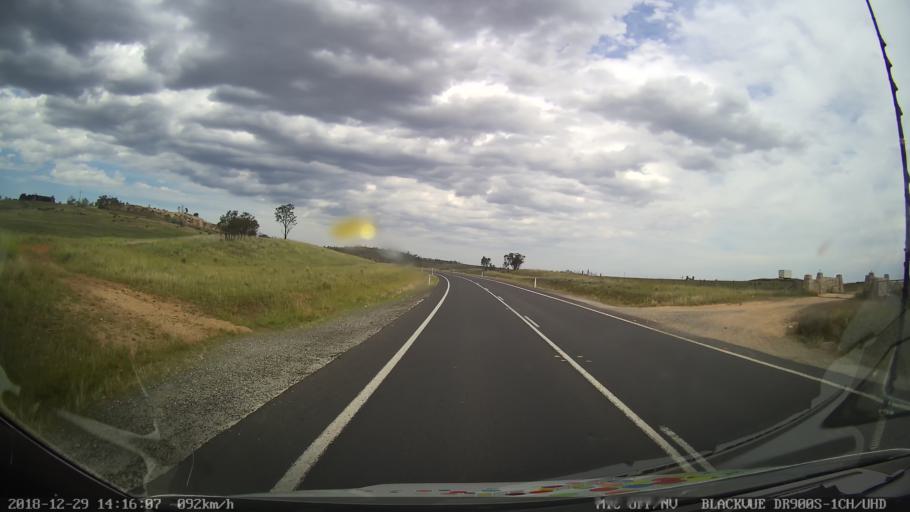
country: AU
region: New South Wales
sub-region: Cooma-Monaro
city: Cooma
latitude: -36.4638
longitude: 149.2463
